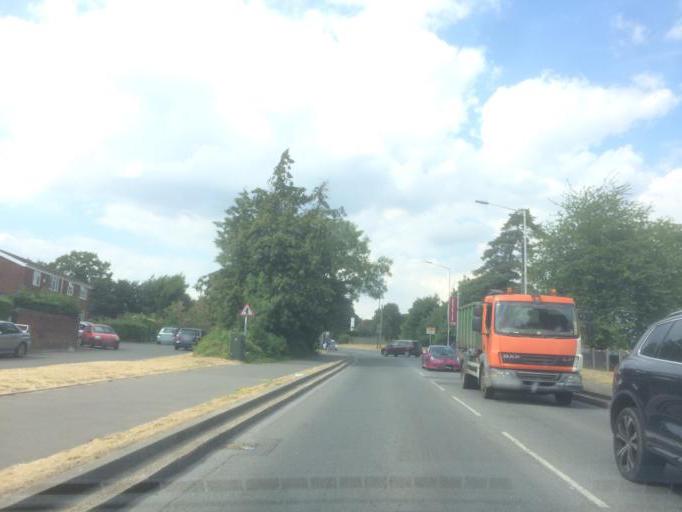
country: GB
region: England
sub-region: Buckinghamshire
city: Farnham Royal
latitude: 51.5331
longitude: -0.6175
